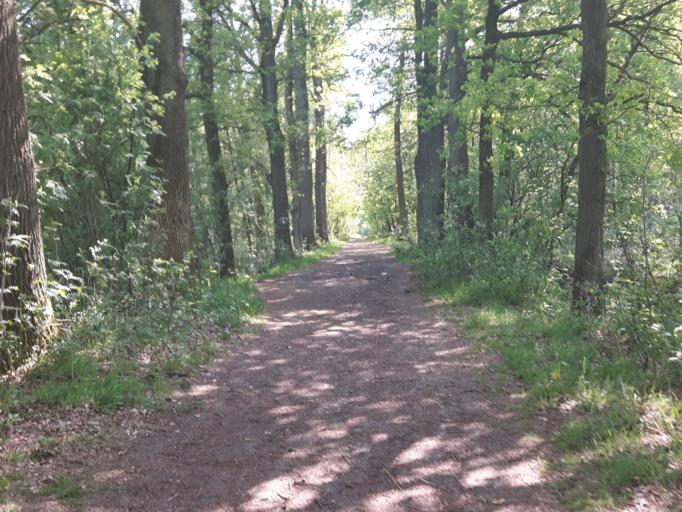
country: NL
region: Overijssel
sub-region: Gemeente Enschede
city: Enschede
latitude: 52.1385
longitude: 6.8714
